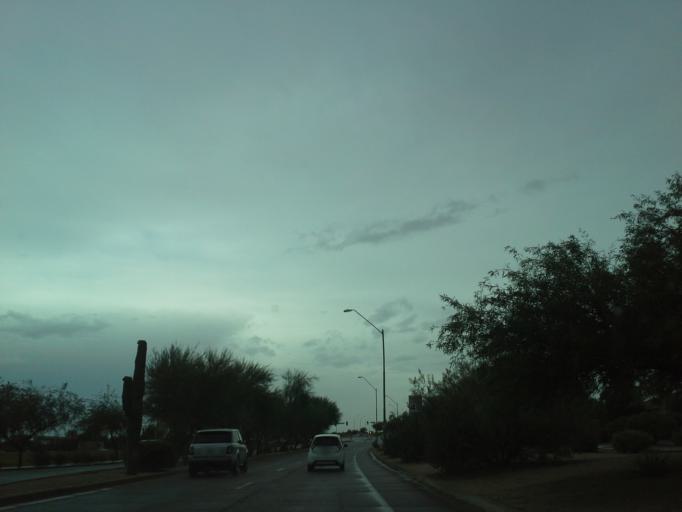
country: US
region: Arizona
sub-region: Maricopa County
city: Paradise Valley
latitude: 33.6427
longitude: -111.9077
